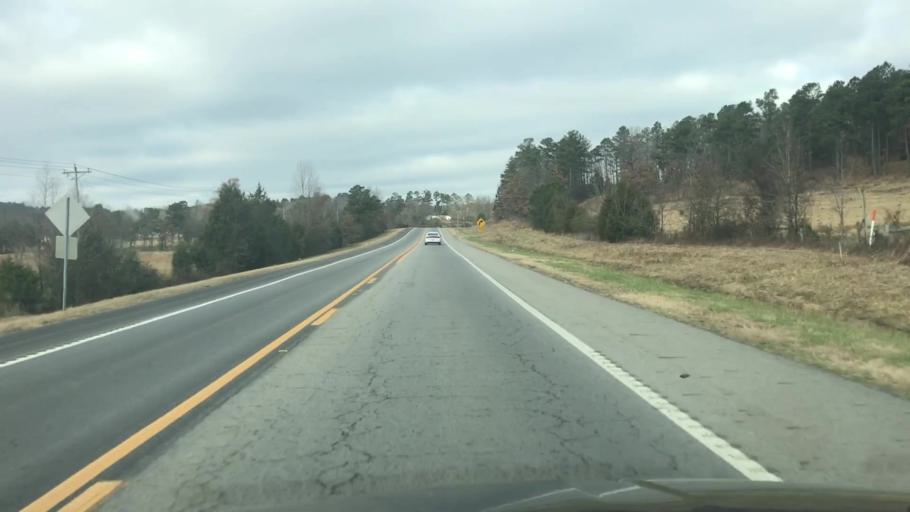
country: US
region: Arkansas
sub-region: Scott County
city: Waldron
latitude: 34.8384
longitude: -94.0487
